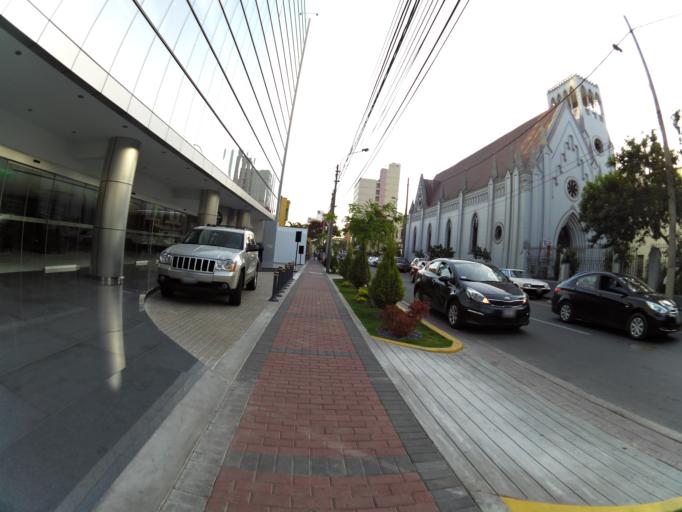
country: PE
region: Lima
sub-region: Lima
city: San Isidro
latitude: -12.1197
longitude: -77.0319
